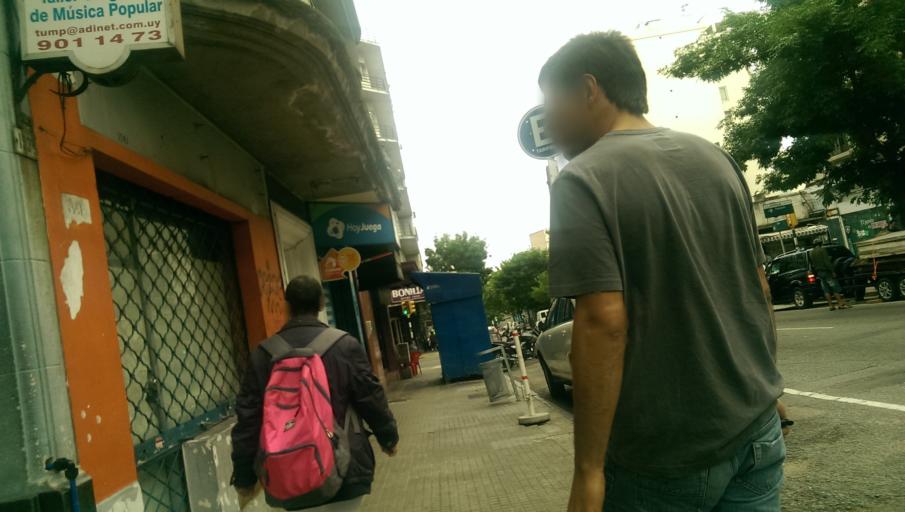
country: UY
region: Montevideo
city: Montevideo
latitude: -34.9021
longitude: -56.1874
